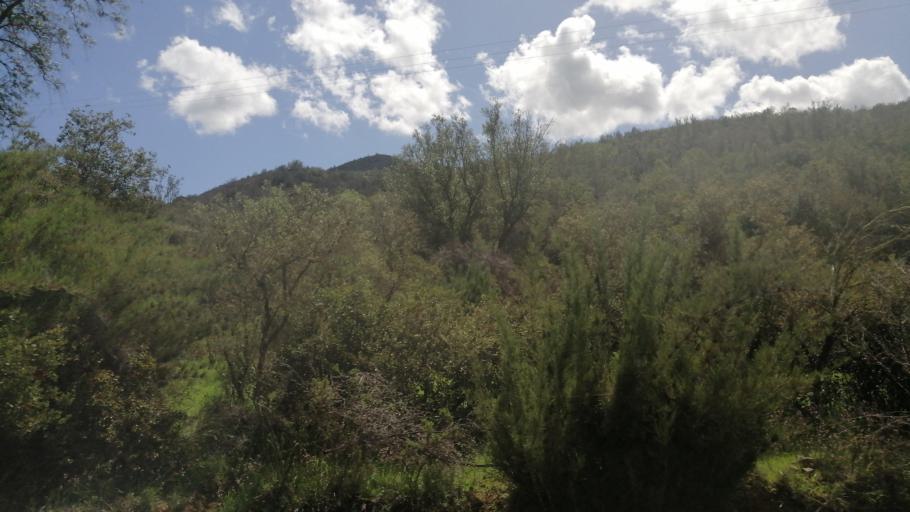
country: CL
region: Valparaiso
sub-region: Provincia de Marga Marga
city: Limache
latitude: -33.1983
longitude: -71.2245
